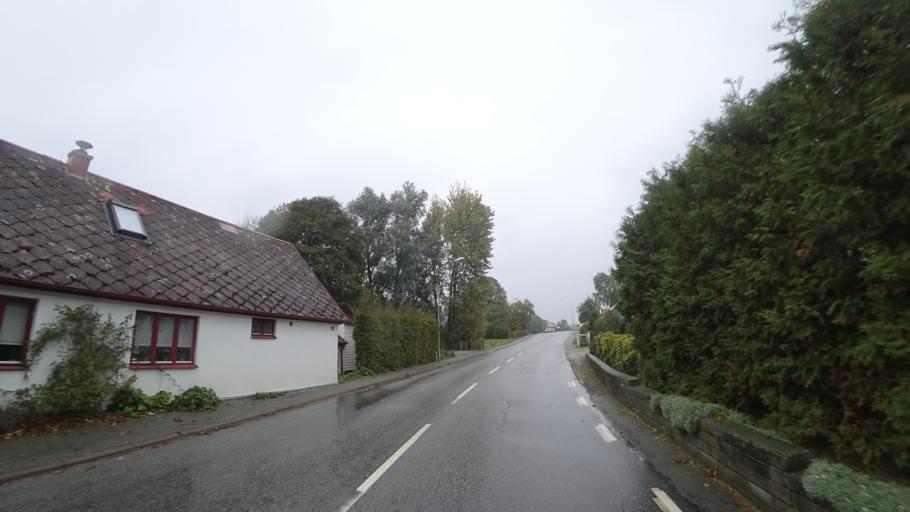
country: SE
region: Skane
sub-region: Kavlinge Kommun
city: Kaevlinge
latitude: 55.8026
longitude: 13.1526
